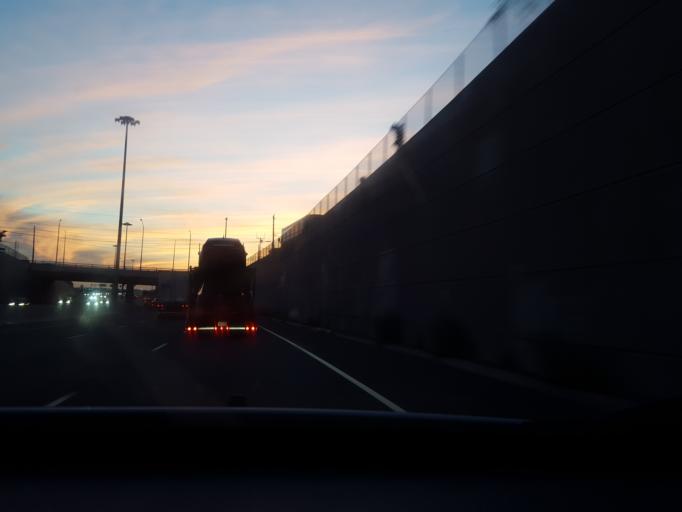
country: CA
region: Ontario
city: Etobicoke
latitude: 43.6986
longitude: -79.5843
